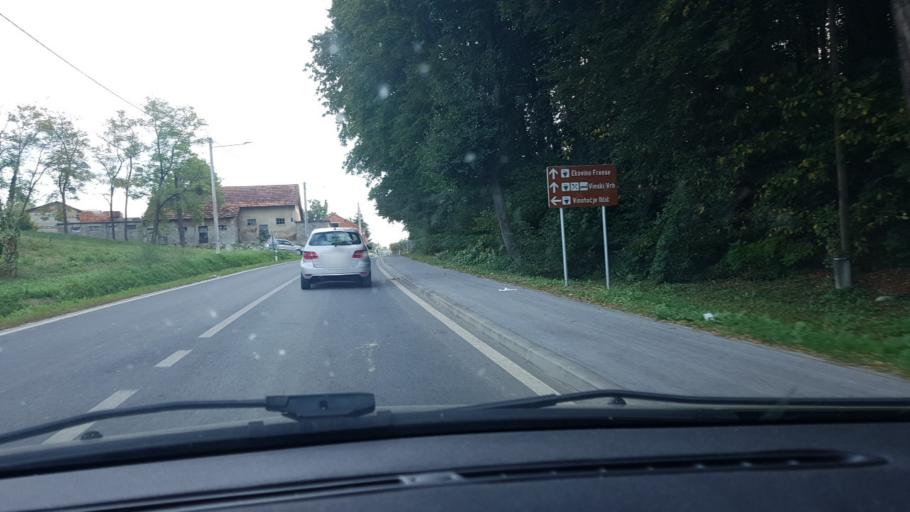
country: HR
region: Krapinsko-Zagorska
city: Zlatar
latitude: 46.1024
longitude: 16.0587
